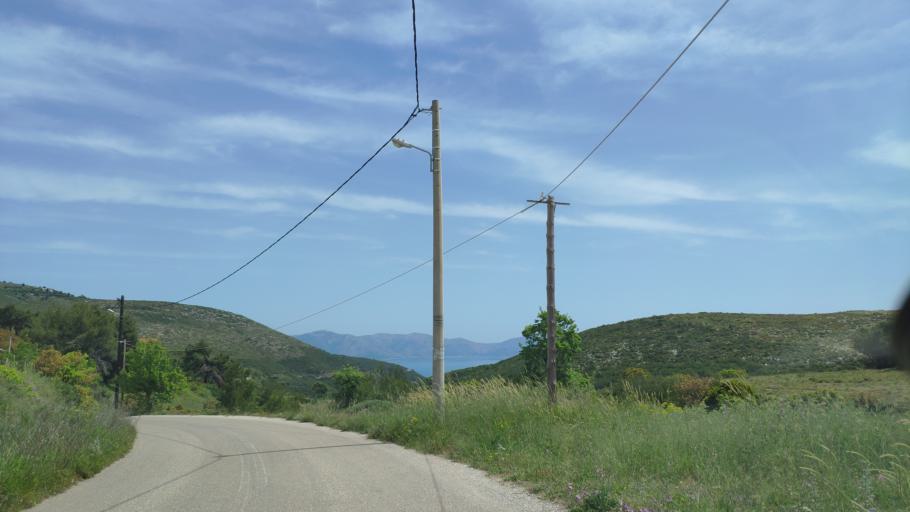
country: GR
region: Attica
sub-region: Nomarchia Anatolikis Attikis
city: Varnavas
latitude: 38.2322
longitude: 23.9410
